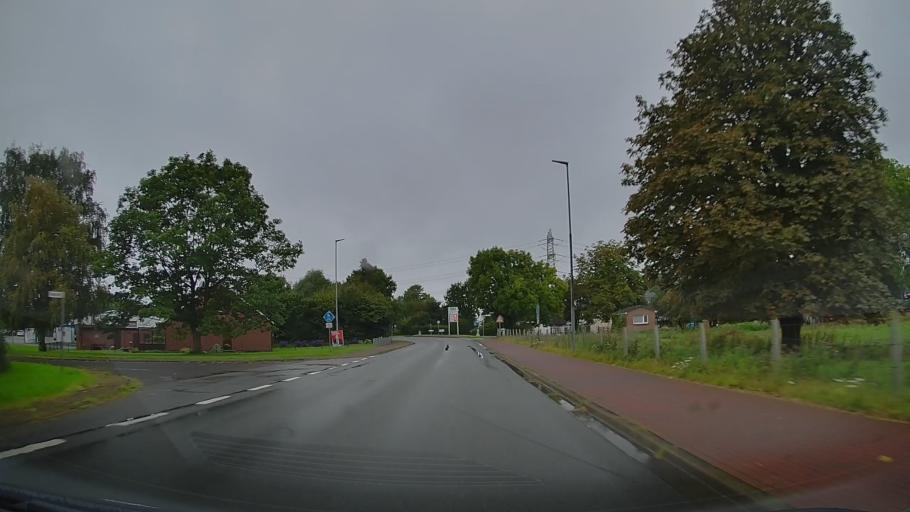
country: DE
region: Schleswig-Holstein
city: Buttel
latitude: 53.8999
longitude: 9.2287
